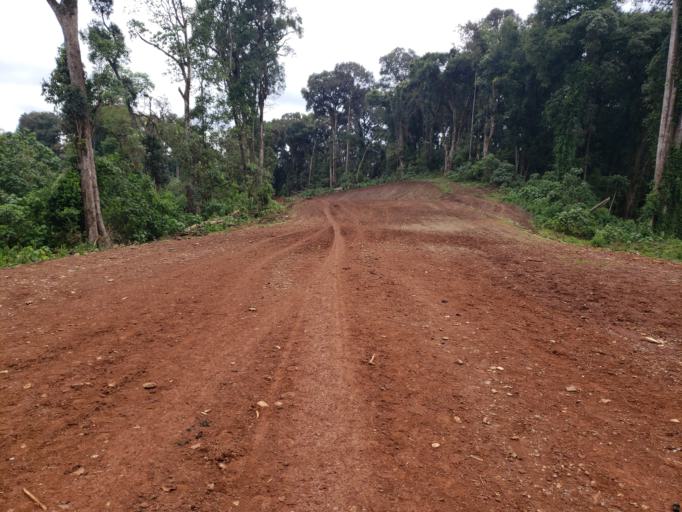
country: ET
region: Oromiya
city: Dodola
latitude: 6.5894
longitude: 39.4121
